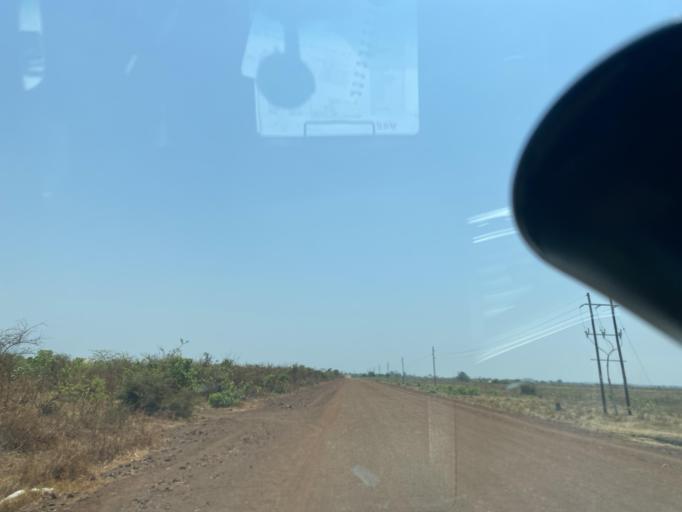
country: ZM
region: Southern
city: Nakambala
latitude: -15.4887
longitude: 27.9008
